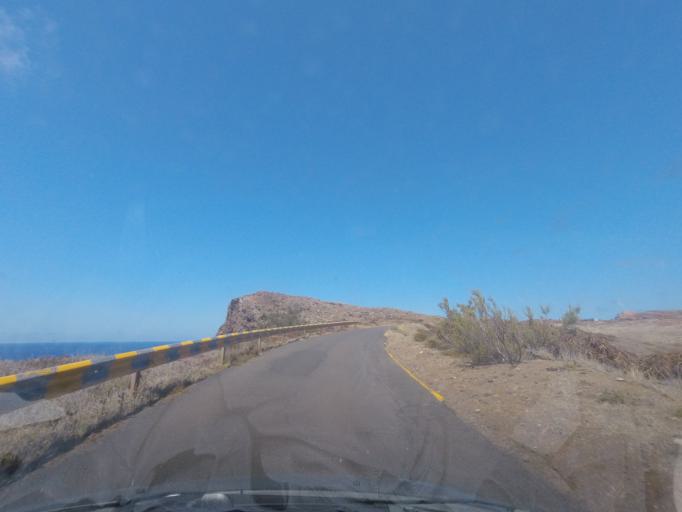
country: PT
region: Madeira
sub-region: Machico
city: Canical
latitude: 32.7489
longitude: -16.7106
